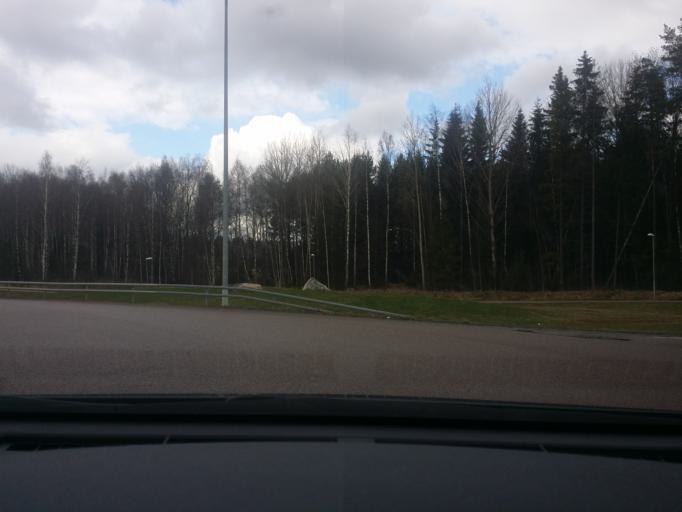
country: SE
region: Vaestmanland
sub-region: Vasteras
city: Vasteras
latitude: 59.6193
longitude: 16.4636
